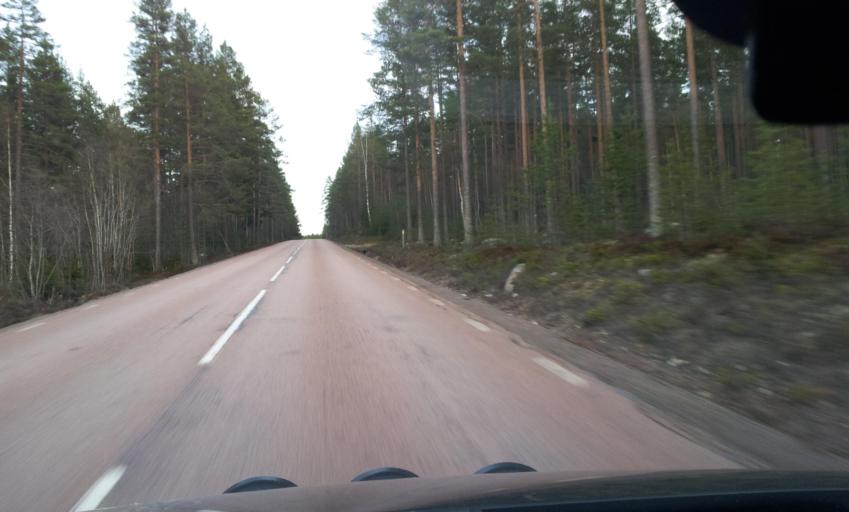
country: SE
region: Gaevleborg
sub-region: Ljusdals Kommun
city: Farila
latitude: 61.9693
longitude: 15.8683
